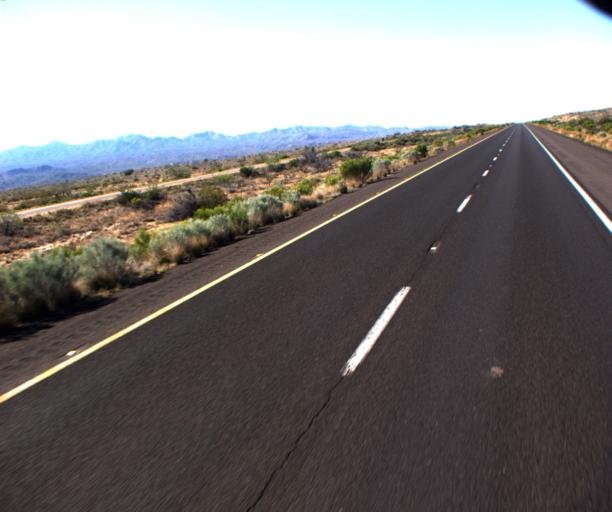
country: US
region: Arizona
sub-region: Mohave County
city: Kingman
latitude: 35.1196
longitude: -113.6669
